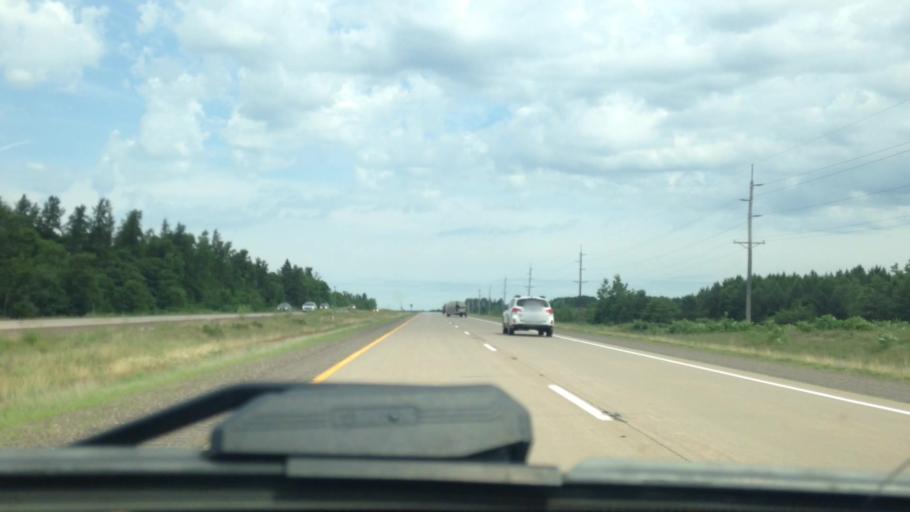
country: US
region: Wisconsin
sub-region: Douglas County
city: Lake Nebagamon
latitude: 46.2300
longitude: -91.8002
